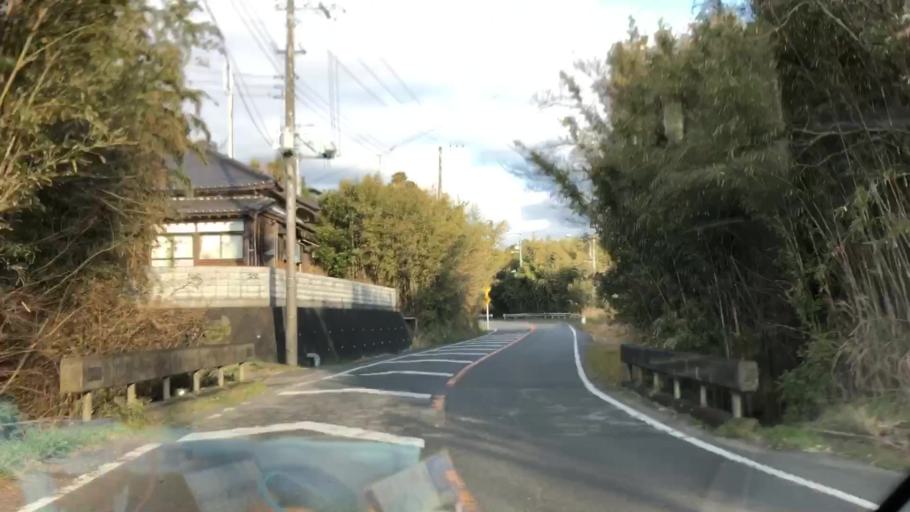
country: JP
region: Chiba
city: Tateyama
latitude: 34.9852
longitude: 139.9425
